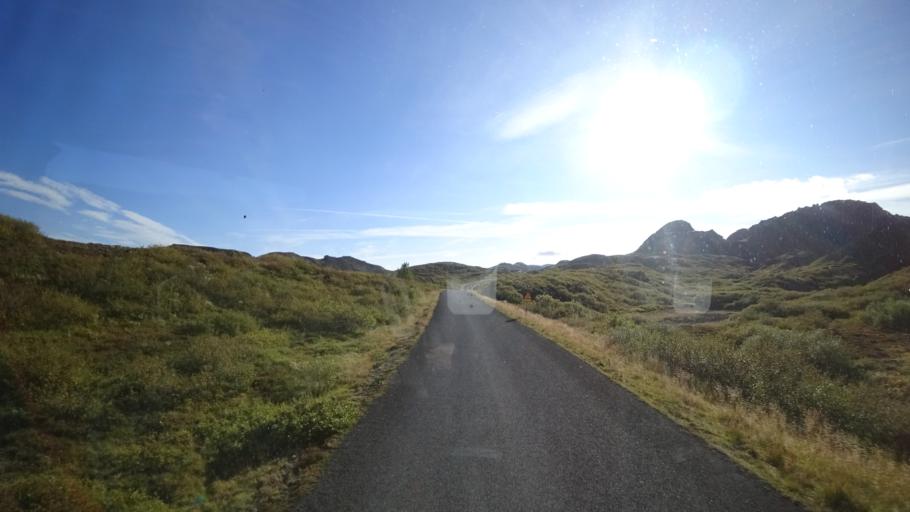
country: IS
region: South
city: Hveragerdi
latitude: 64.1531
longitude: -21.2550
